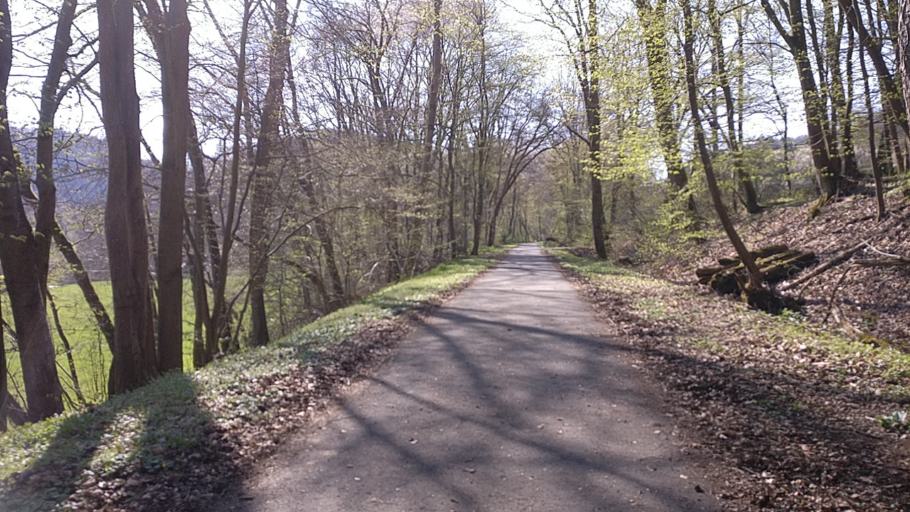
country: DE
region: Rheinland-Pfalz
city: Peterslahr
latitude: 50.6181
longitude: 7.4485
